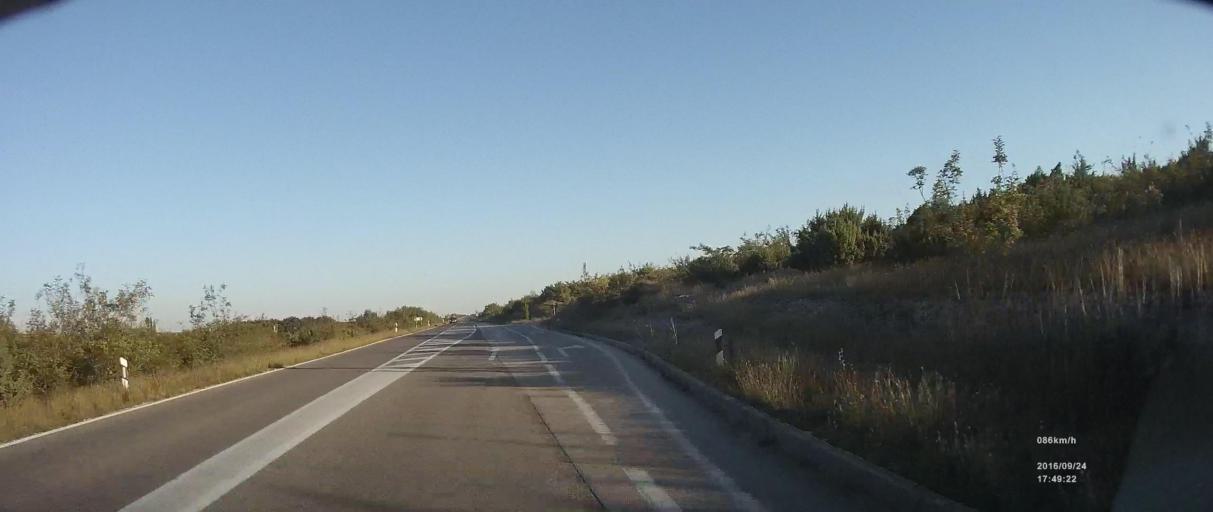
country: HR
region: Zadarska
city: Polaca
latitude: 44.0548
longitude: 15.5490
